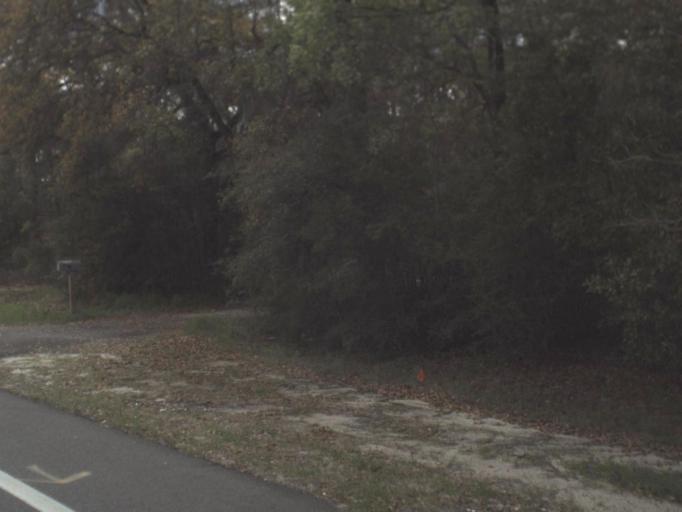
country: US
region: Florida
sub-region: Wakulla County
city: Crawfordville
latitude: 30.2162
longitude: -84.3628
